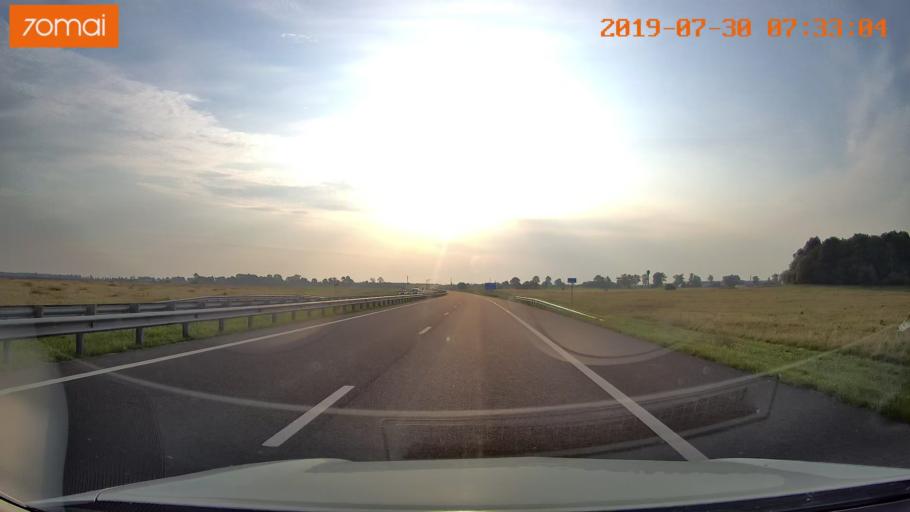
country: RU
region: Kaliningrad
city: Gvardeysk
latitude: 54.6676
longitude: 21.0362
